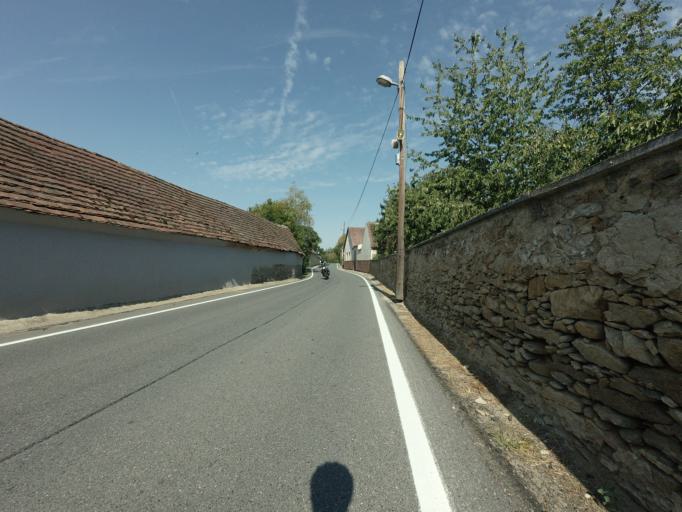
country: CZ
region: Jihocesky
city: Bernartice
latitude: 49.3822
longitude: 14.3652
